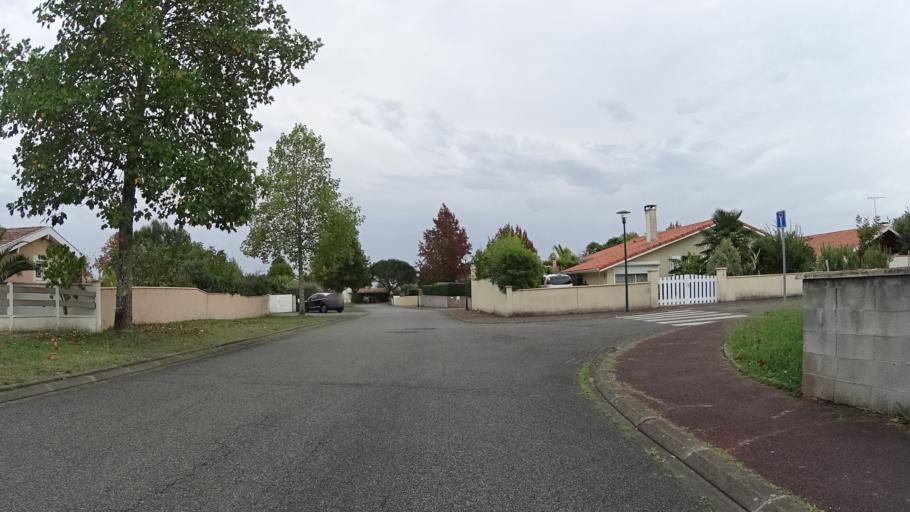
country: FR
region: Aquitaine
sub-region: Departement des Landes
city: Saint-Paul-les-Dax
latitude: 43.7293
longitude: -1.0794
